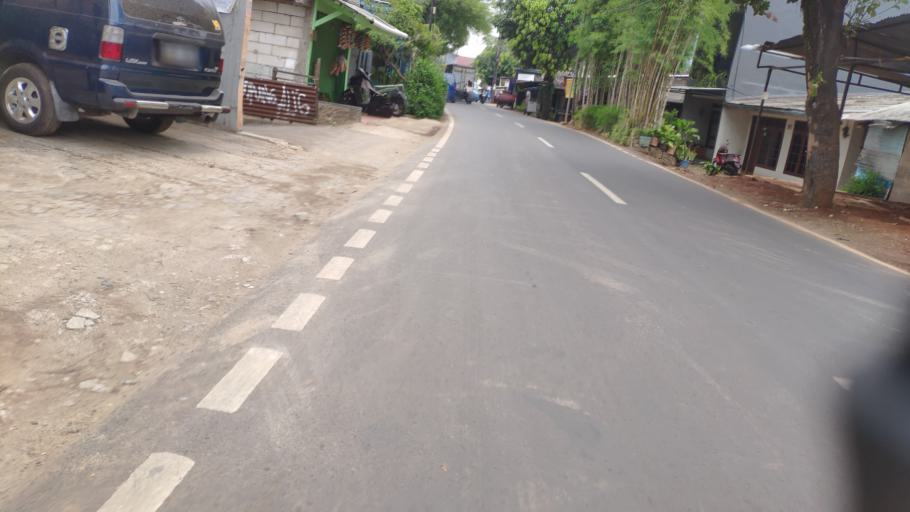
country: ID
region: West Java
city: Depok
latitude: -6.3462
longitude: 106.8245
